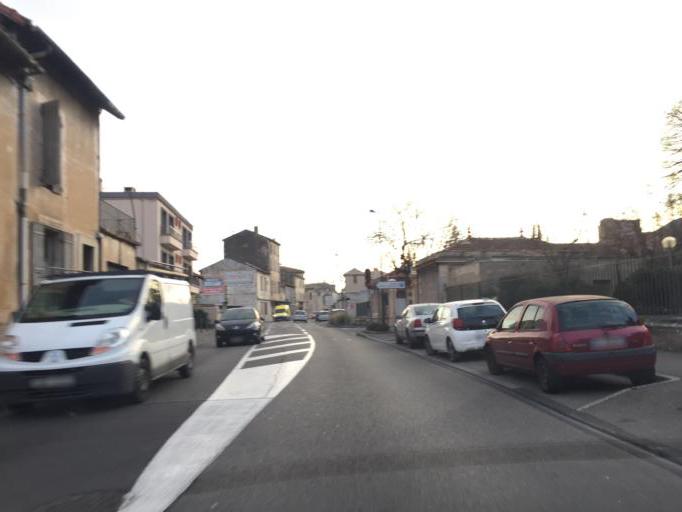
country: FR
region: Provence-Alpes-Cote d'Azur
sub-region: Departement du Vaucluse
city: Cavaillon
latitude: 43.8406
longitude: 5.0380
